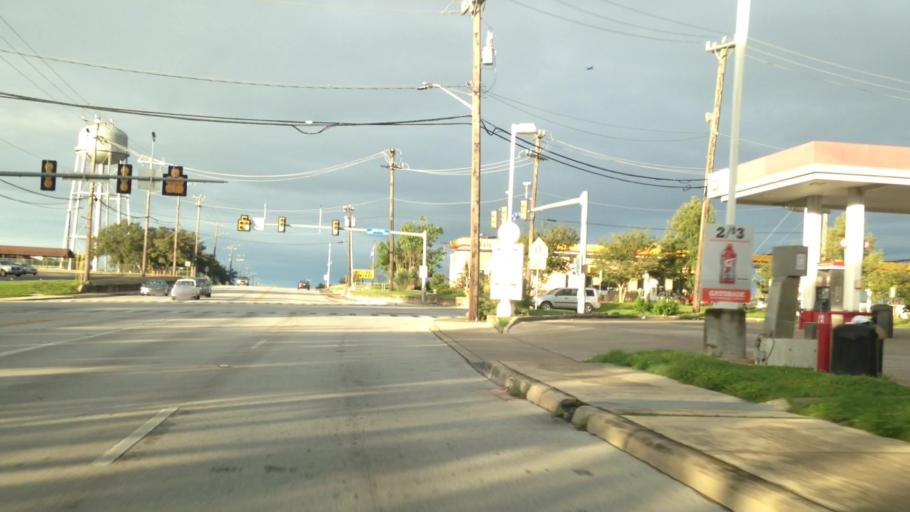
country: US
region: Texas
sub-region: Bexar County
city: Live Oak
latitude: 29.5875
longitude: -98.3771
